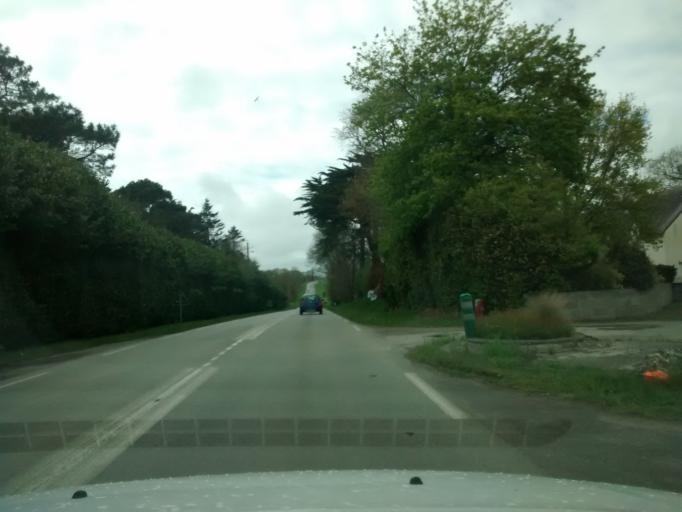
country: FR
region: Brittany
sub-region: Departement du Morbihan
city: Gestel
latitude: 47.7810
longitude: -3.4420
